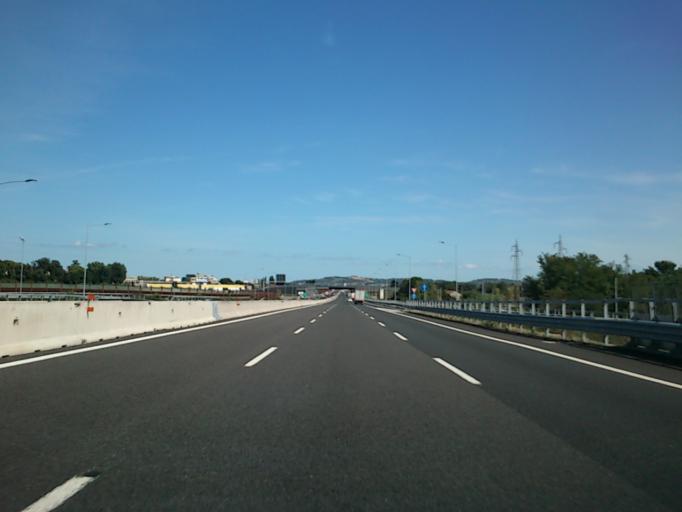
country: IT
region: The Marches
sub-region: Provincia di Pesaro e Urbino
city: Villa Ceccolini
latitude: 43.8991
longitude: 12.8437
